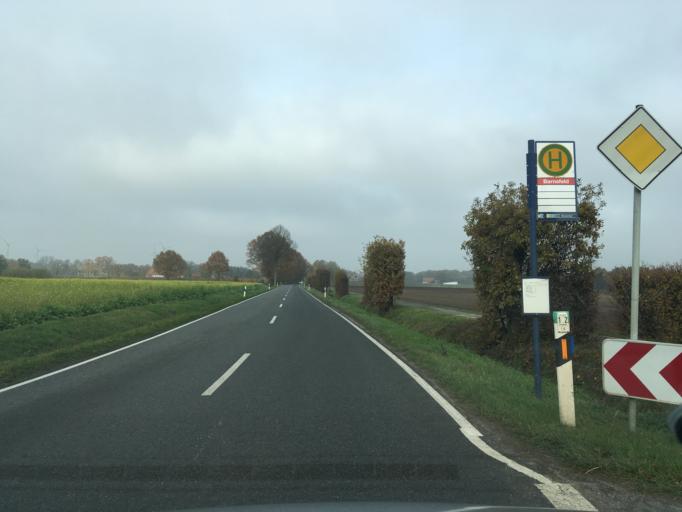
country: DE
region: North Rhine-Westphalia
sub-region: Regierungsbezirk Munster
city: Sudlohn
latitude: 51.9120
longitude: 6.9175
